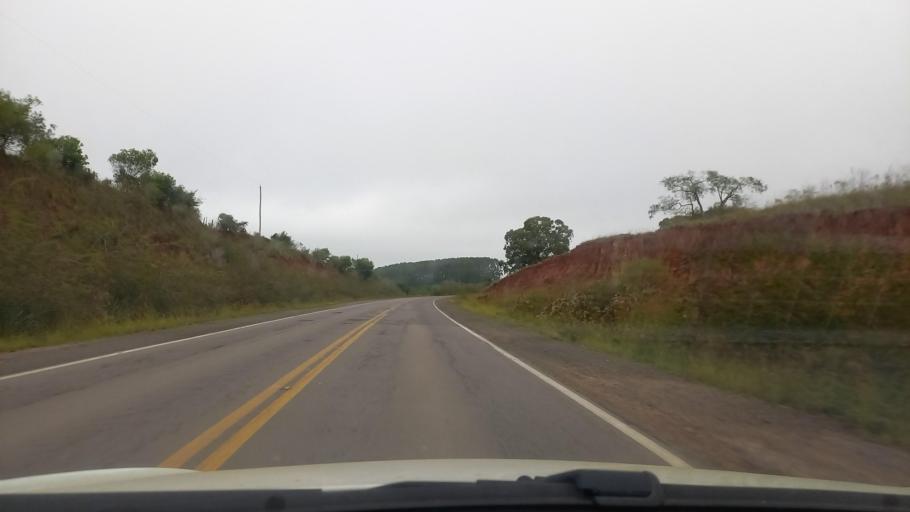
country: BR
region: Rio Grande do Sul
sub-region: Rosario Do Sul
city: Rosario do Sul
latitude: -30.1348
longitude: -54.6593
